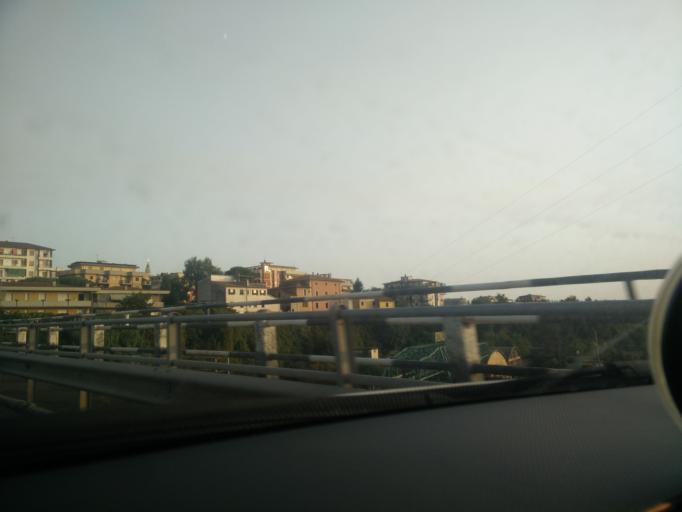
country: IT
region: Tuscany
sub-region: Provincia di Massa-Carrara
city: Massa
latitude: 44.0406
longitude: 10.1385
